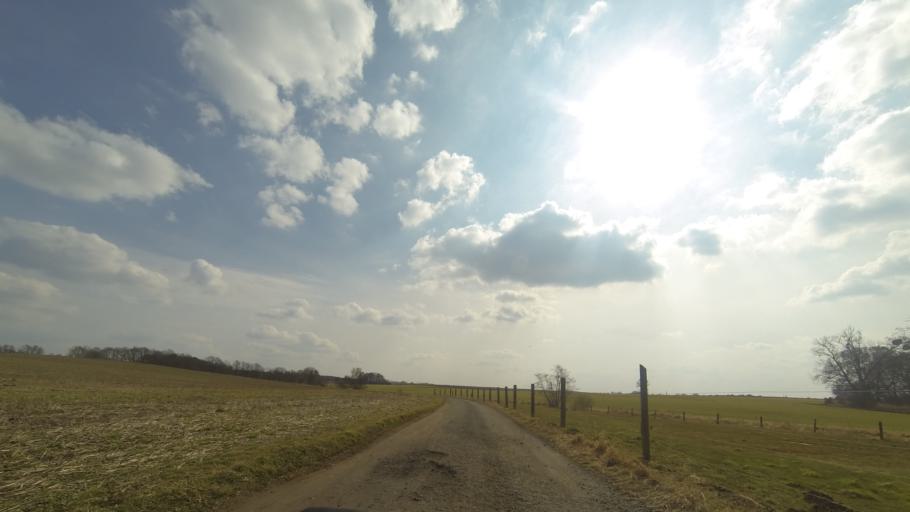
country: DE
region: Saxony
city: Albertstadt
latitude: 51.1422
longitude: 13.7425
